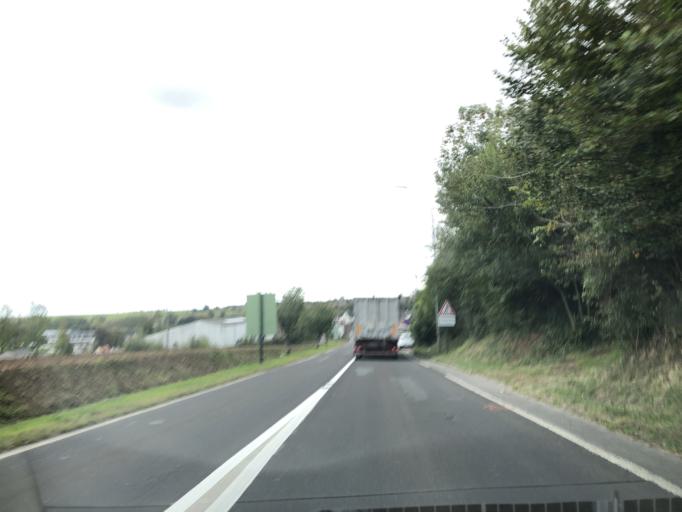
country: FR
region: Nord-Pas-de-Calais
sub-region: Departement du Pas-de-Calais
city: Fruges
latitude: 50.5208
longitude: 2.1330
